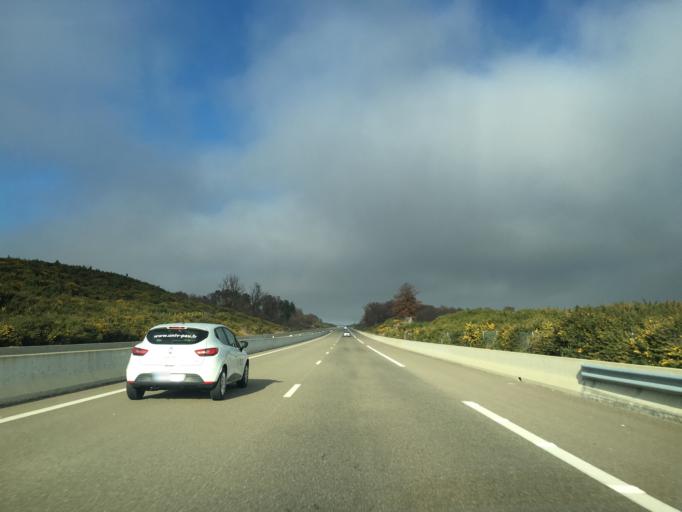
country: FR
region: Aquitaine
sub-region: Departement des Landes
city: Villeneuve-de-Marsan
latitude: 43.8081
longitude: -0.3055
